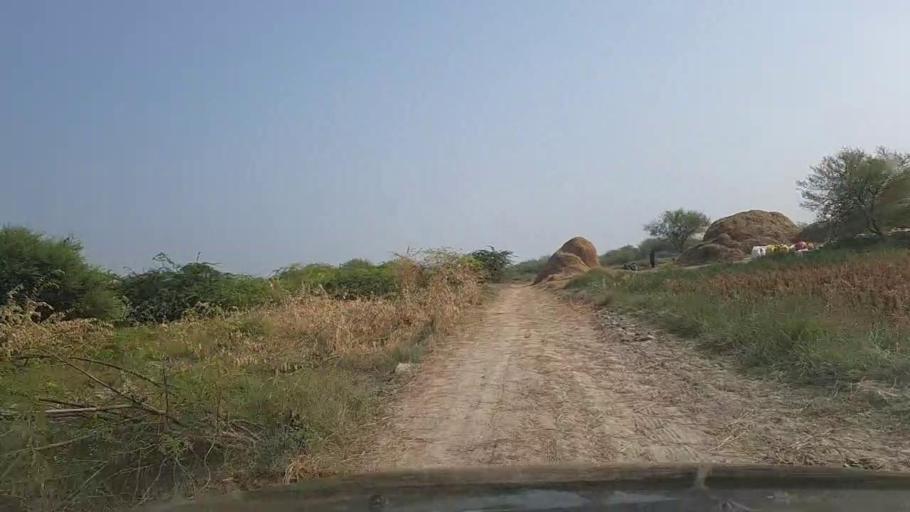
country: PK
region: Sindh
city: Mirpur Batoro
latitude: 24.6788
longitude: 68.2416
